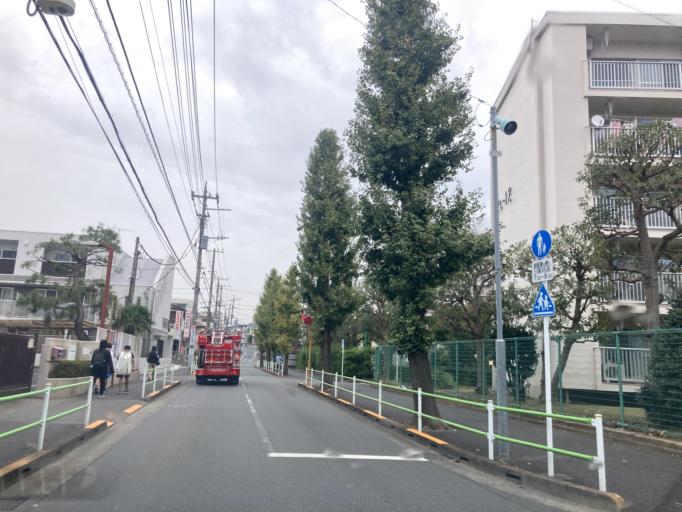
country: JP
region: Tokyo
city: Chofugaoka
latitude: 35.6422
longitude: 139.5558
